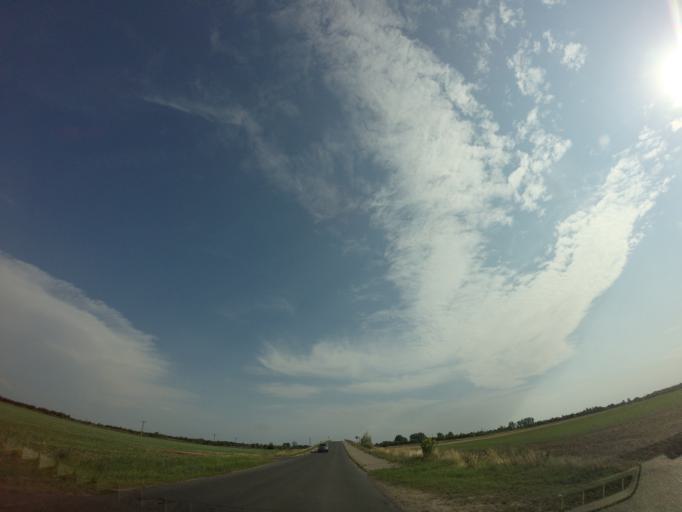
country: PL
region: West Pomeranian Voivodeship
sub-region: Powiat stargardzki
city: Stargard Szczecinski
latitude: 53.3086
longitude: 15.0461
